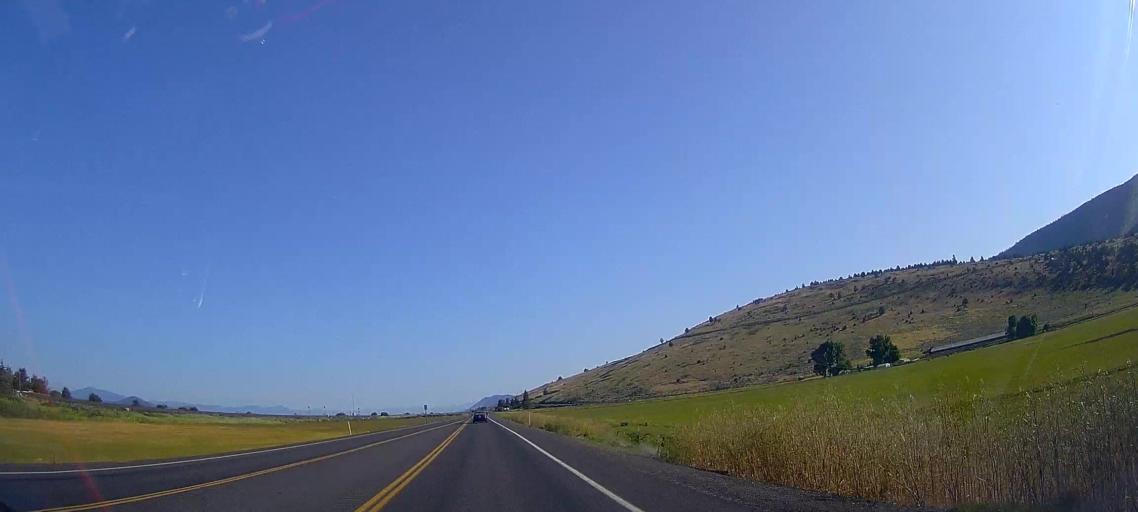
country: US
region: Oregon
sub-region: Klamath County
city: Klamath Falls
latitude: 42.2833
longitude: -121.8134
